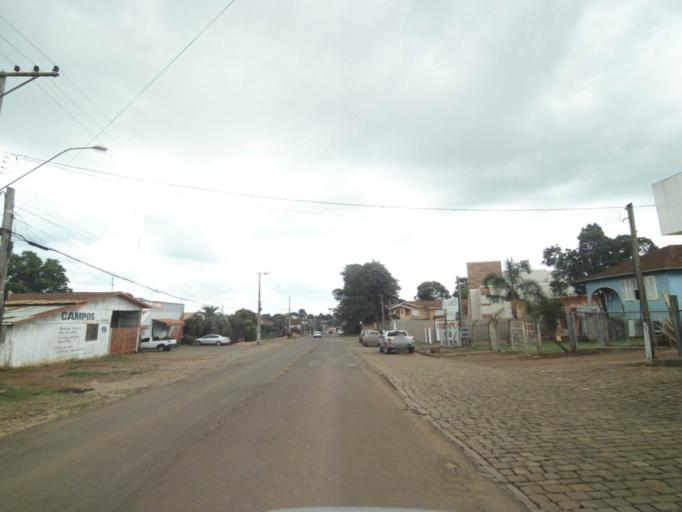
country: BR
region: Rio Grande do Sul
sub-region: Lagoa Vermelha
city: Lagoa Vermelha
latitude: -28.2128
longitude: -51.5249
